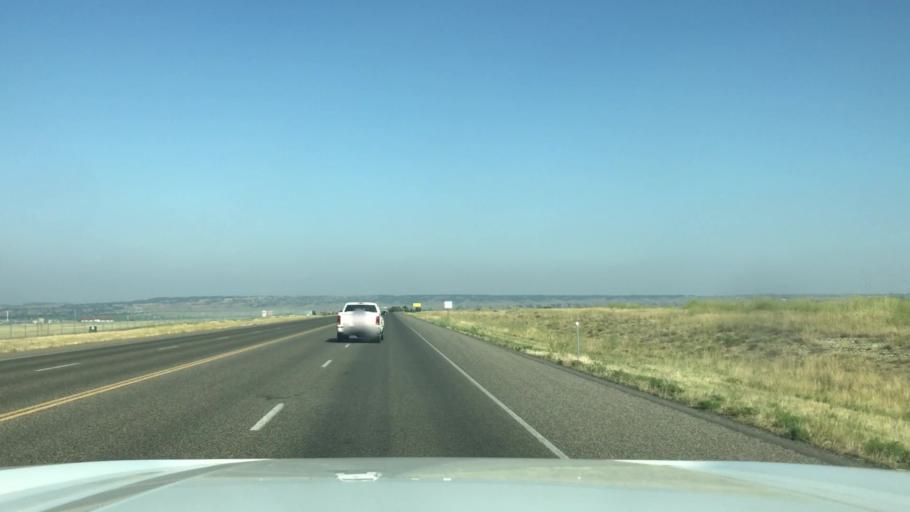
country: US
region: Montana
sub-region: Yellowstone County
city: Billings
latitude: 45.8000
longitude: -108.5162
